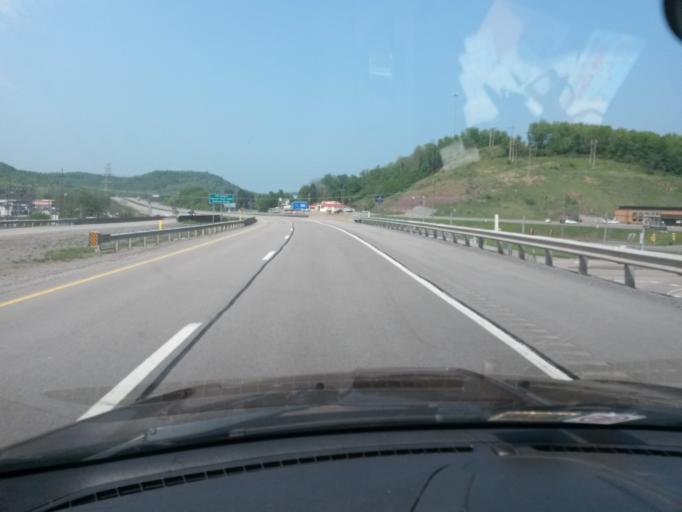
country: US
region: West Virginia
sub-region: Upshur County
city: Buckhannon
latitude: 39.0019
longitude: -80.2314
